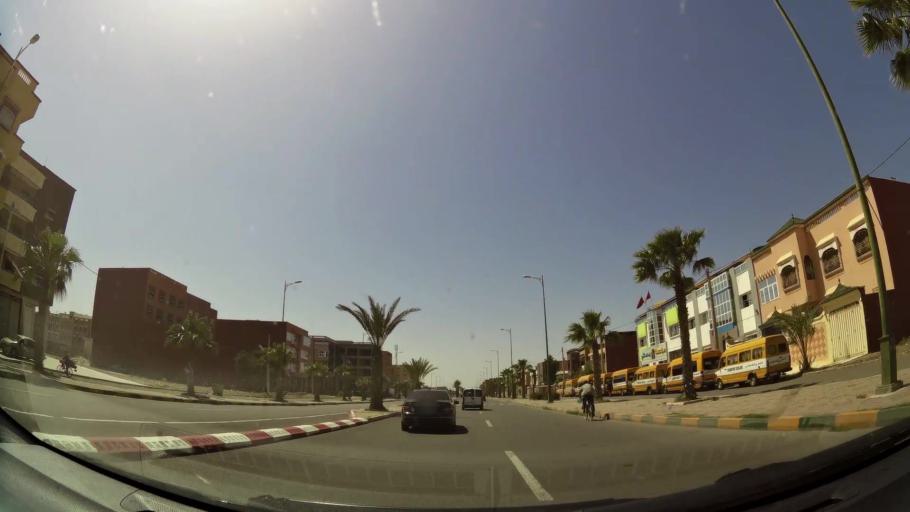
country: MA
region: Souss-Massa-Draa
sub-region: Inezgane-Ait Mellou
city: Inezgane
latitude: 30.3231
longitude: -9.5036
